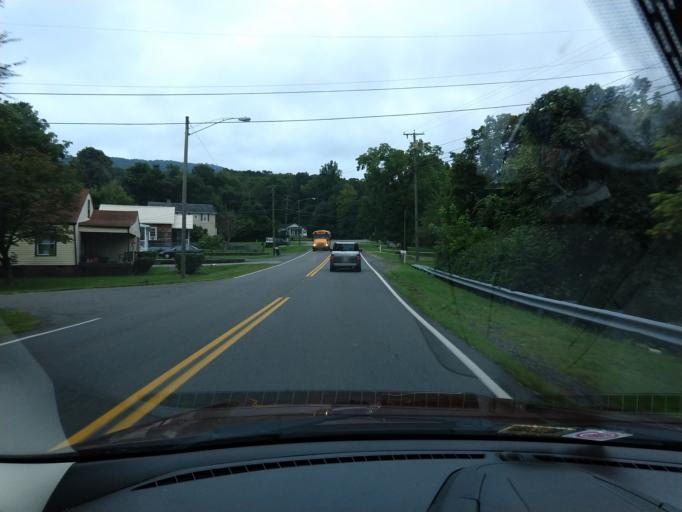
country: US
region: Virginia
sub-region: City of Covington
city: Fairlawn
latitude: 37.7552
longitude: -79.9872
